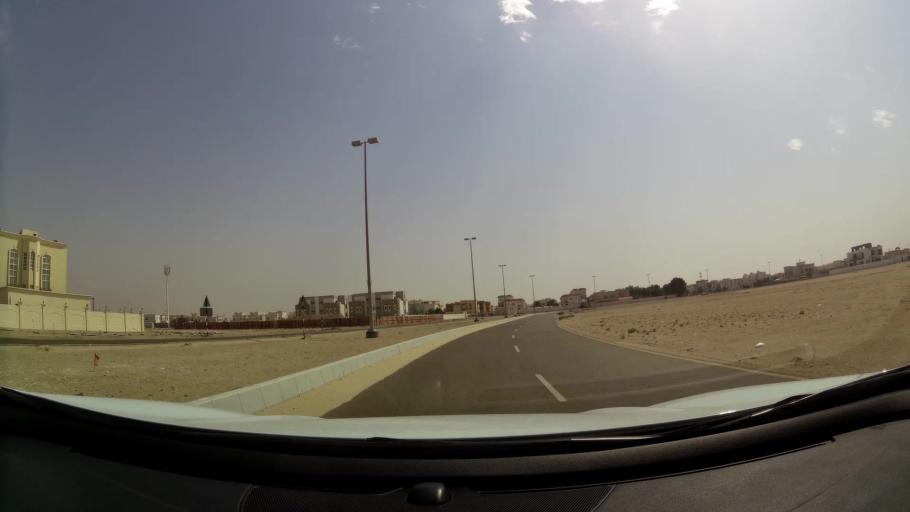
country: AE
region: Abu Dhabi
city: Abu Dhabi
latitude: 24.3350
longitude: 54.5667
